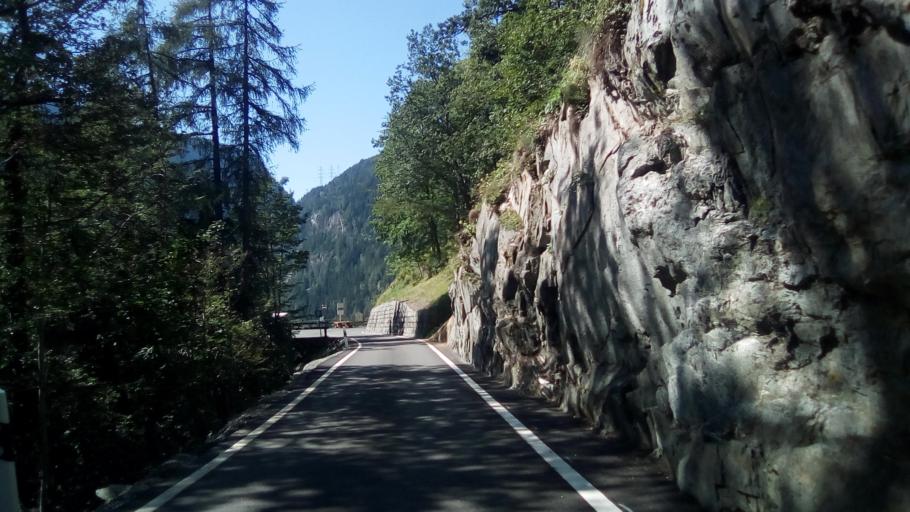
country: CH
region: Valais
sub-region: Saint-Maurice District
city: Salvan
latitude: 46.1045
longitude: 7.0019
